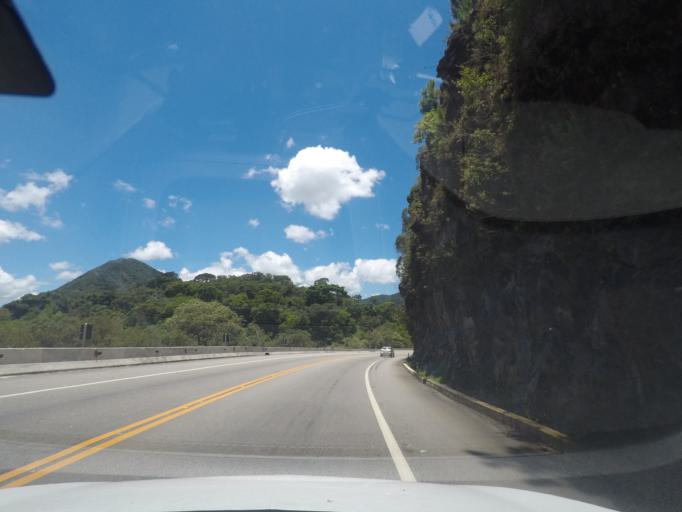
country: BR
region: Rio de Janeiro
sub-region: Teresopolis
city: Teresopolis
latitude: -22.4584
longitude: -42.9763
